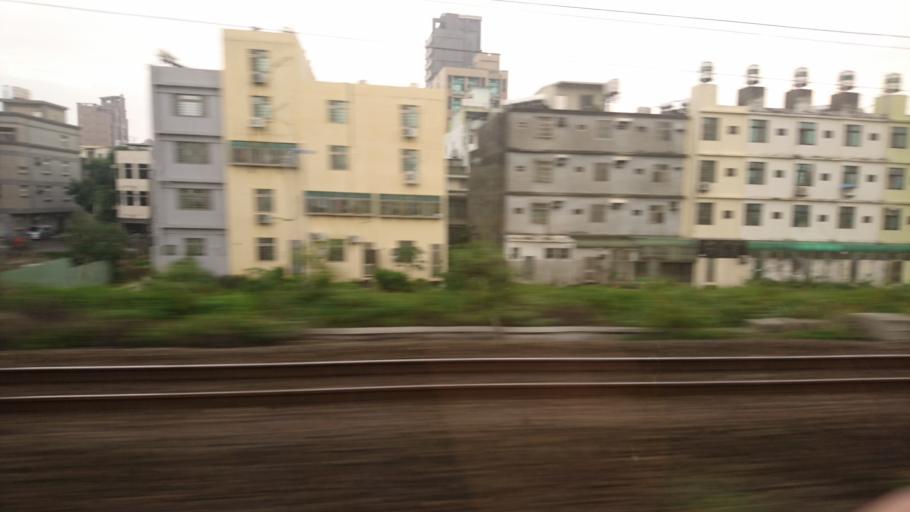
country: TW
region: Taiwan
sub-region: Hsinchu
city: Zhubei
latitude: 24.8330
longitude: 121.0047
